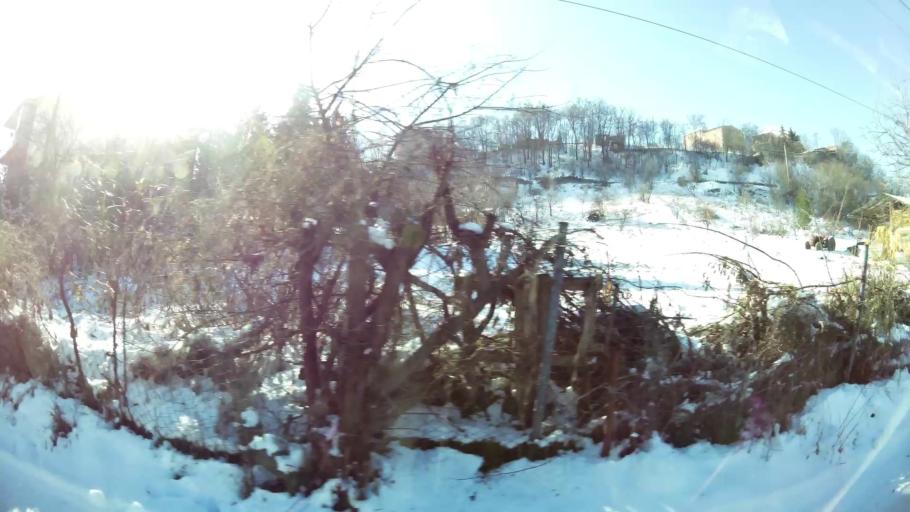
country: MK
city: Ljubin
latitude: 42.0031
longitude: 21.3102
